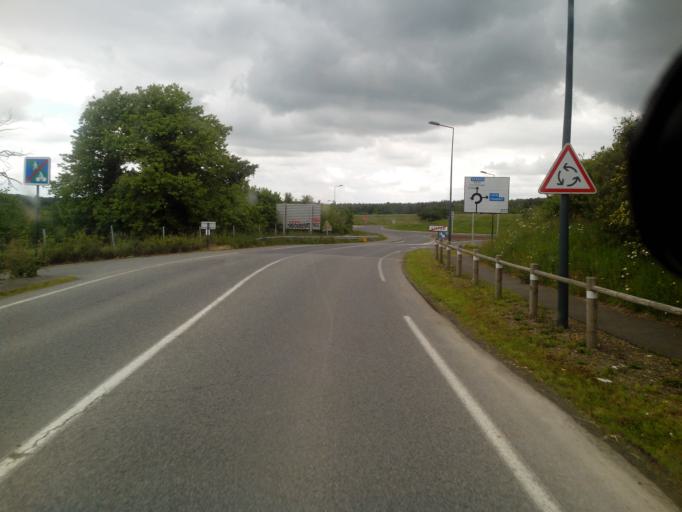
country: FR
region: Brittany
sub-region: Departement d'Ille-et-Vilaine
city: Liffre
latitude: 48.2199
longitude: -1.4973
